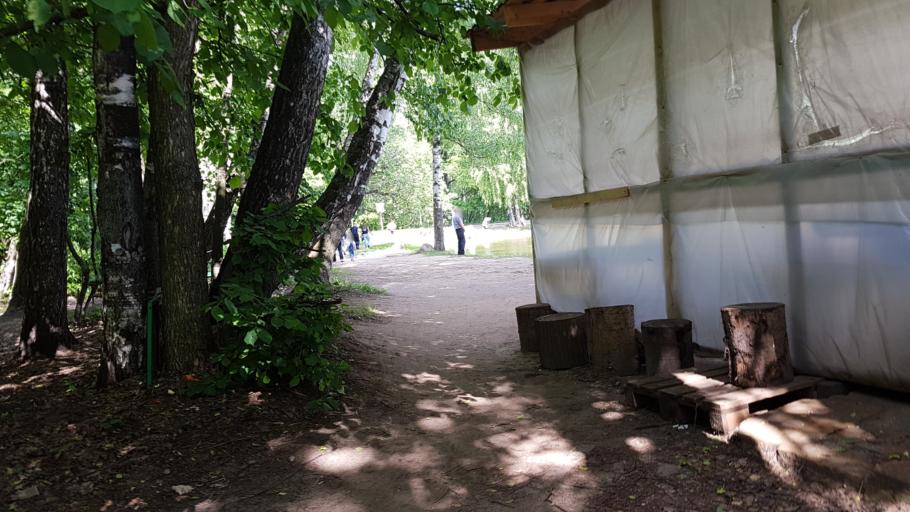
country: RU
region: Moskovskaya
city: Izmaylovo
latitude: 55.7750
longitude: 37.7741
